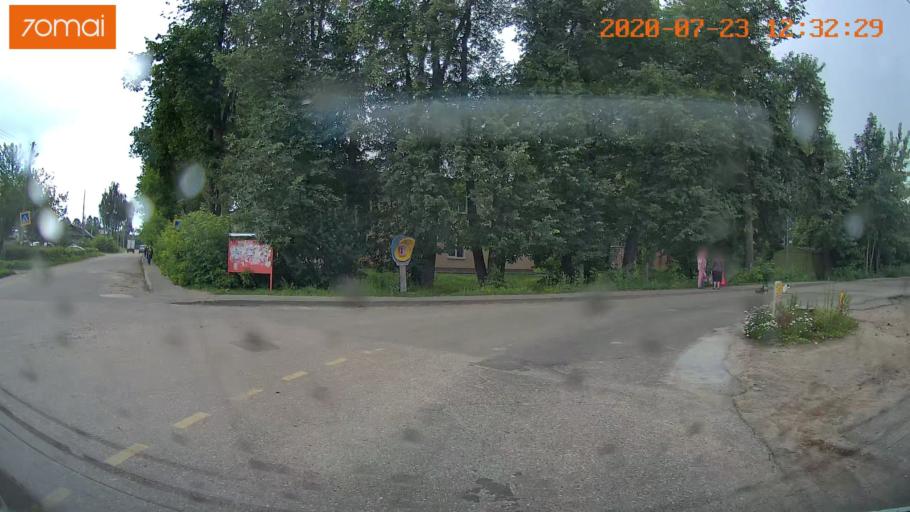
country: RU
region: Ivanovo
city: Bogorodskoye
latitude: 57.0463
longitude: 41.0061
